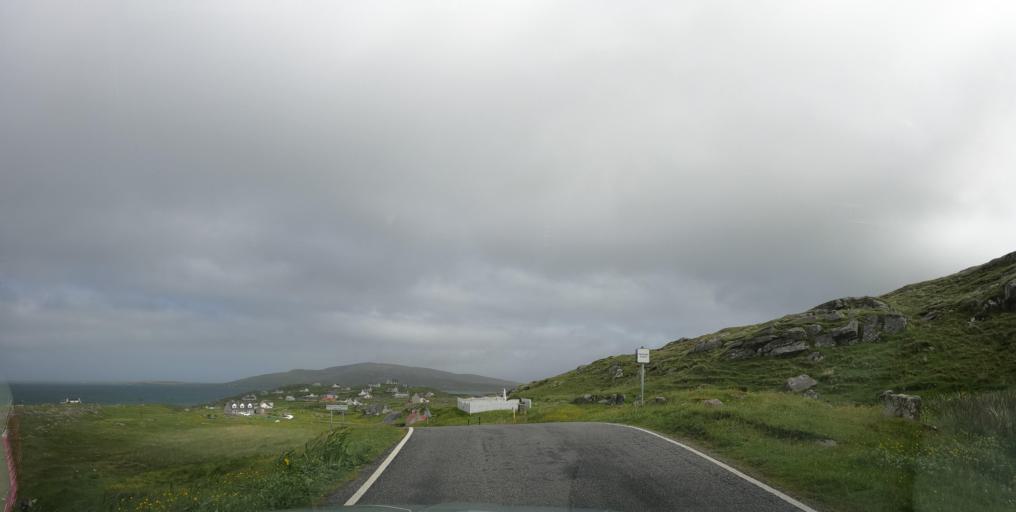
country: GB
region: Scotland
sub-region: Eilean Siar
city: Isle of South Uist
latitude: 57.0804
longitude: -7.3025
